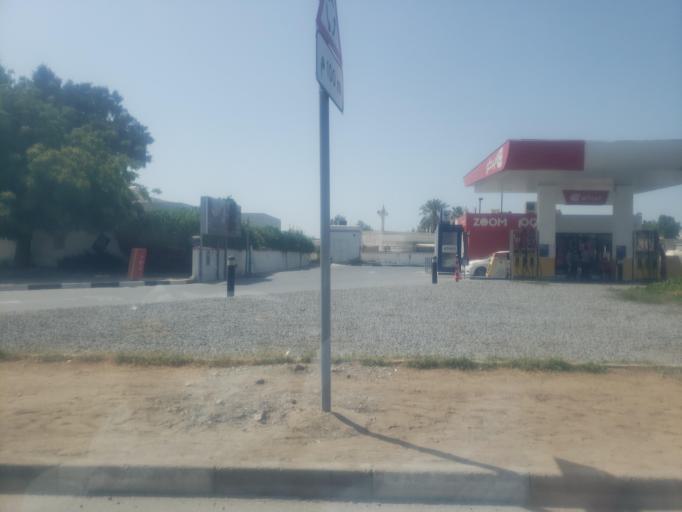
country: AE
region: Ra's al Khaymah
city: Ras al-Khaimah
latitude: 25.8064
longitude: 55.9620
